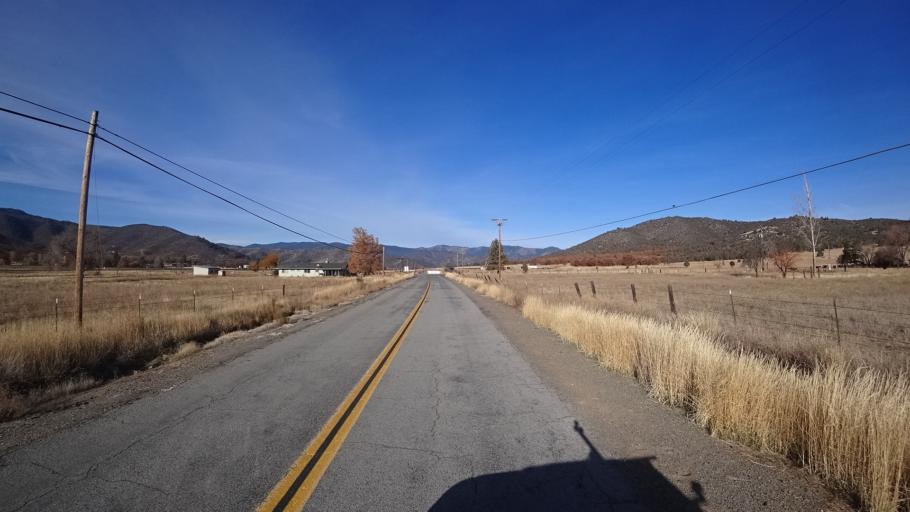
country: US
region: California
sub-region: Siskiyou County
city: Yreka
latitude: 41.6700
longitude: -122.6105
